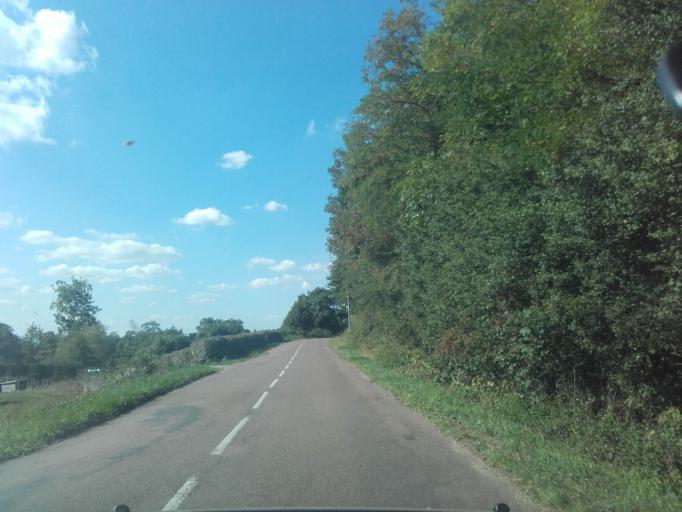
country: FR
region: Bourgogne
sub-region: Departement de Saone-et-Loire
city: Epinac
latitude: 46.9908
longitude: 4.5097
